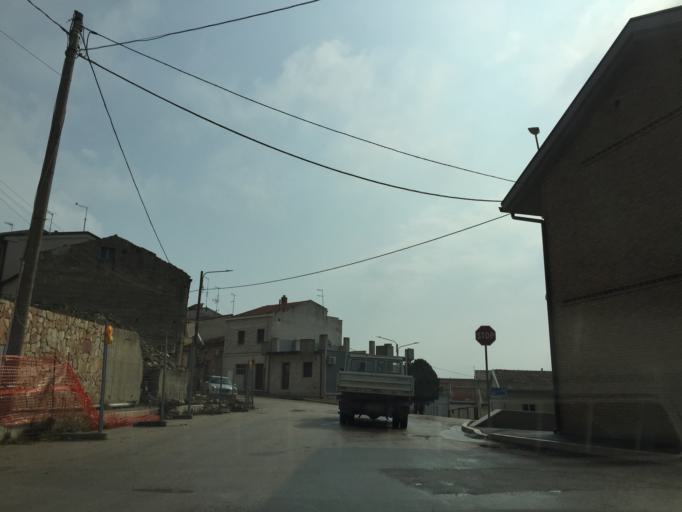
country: IT
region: Apulia
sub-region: Provincia di Foggia
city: Troia
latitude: 41.3586
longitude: 15.3021
